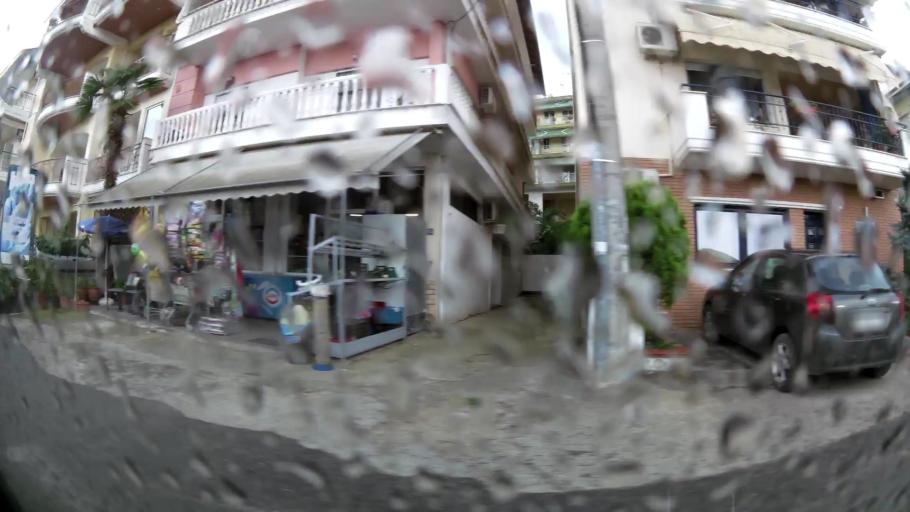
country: GR
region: Central Macedonia
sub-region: Nomos Imathias
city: Veroia
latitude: 40.5246
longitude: 22.1964
